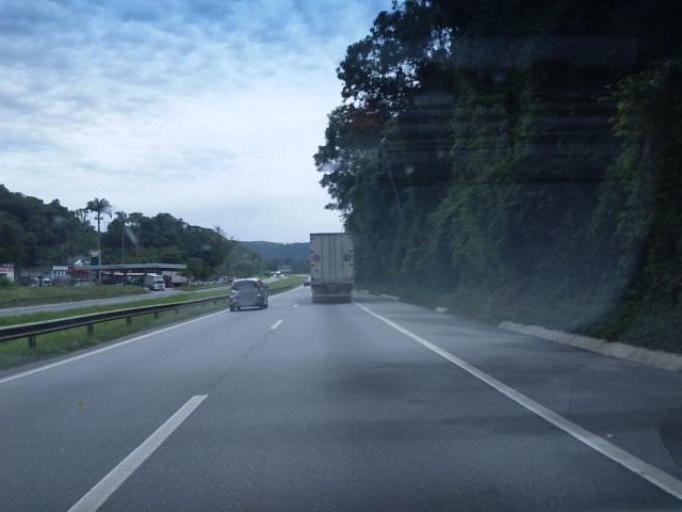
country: BR
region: Sao Paulo
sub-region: Miracatu
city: Miracatu
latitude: -24.1964
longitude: -47.3650
